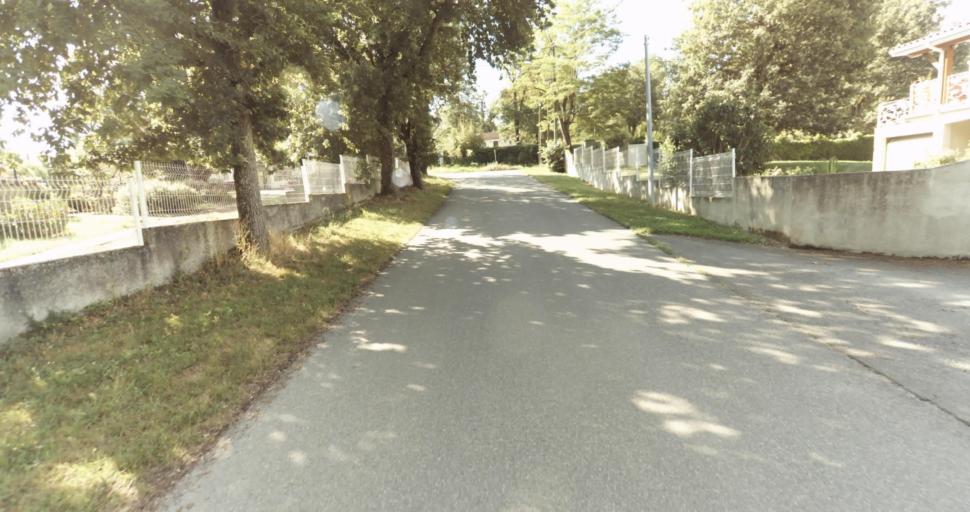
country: FR
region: Midi-Pyrenees
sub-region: Departement de la Haute-Garonne
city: Fontenilles
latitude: 43.5627
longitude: 1.2180
